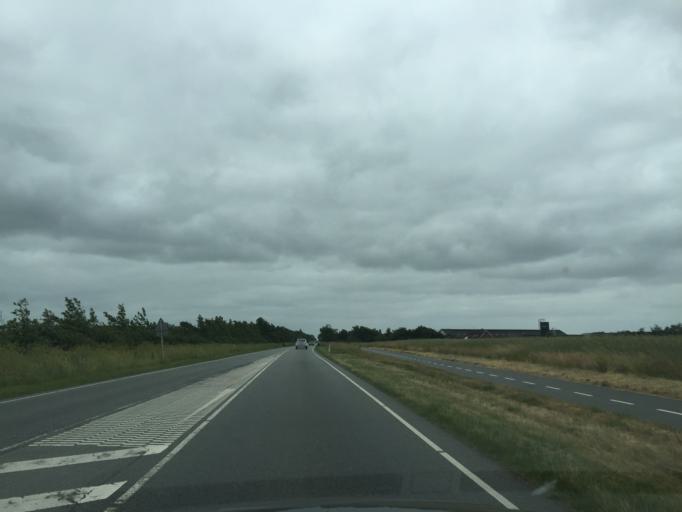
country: DK
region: South Denmark
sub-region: Esbjerg Kommune
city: Ribe
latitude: 55.3134
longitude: 8.7501
